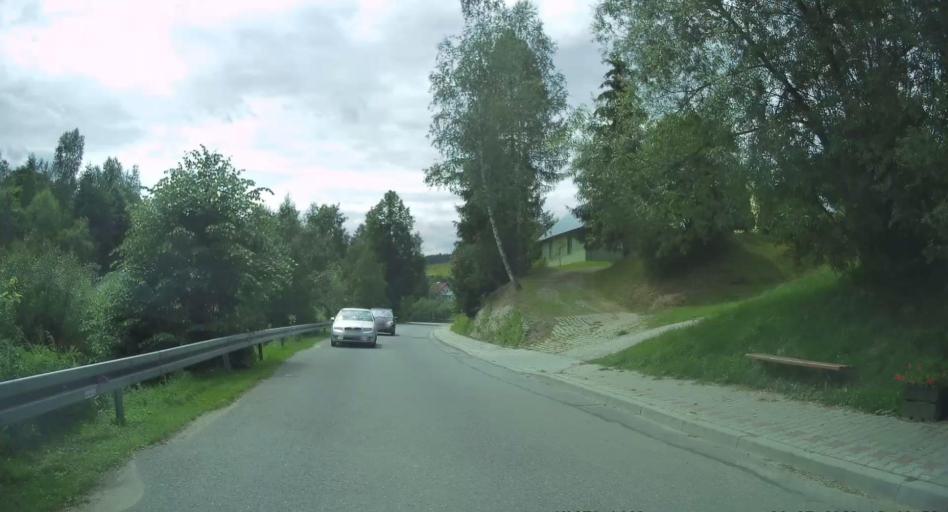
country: PL
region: Lesser Poland Voivodeship
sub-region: Powiat nowosadecki
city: Muszyna
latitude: 49.3787
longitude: 20.8923
